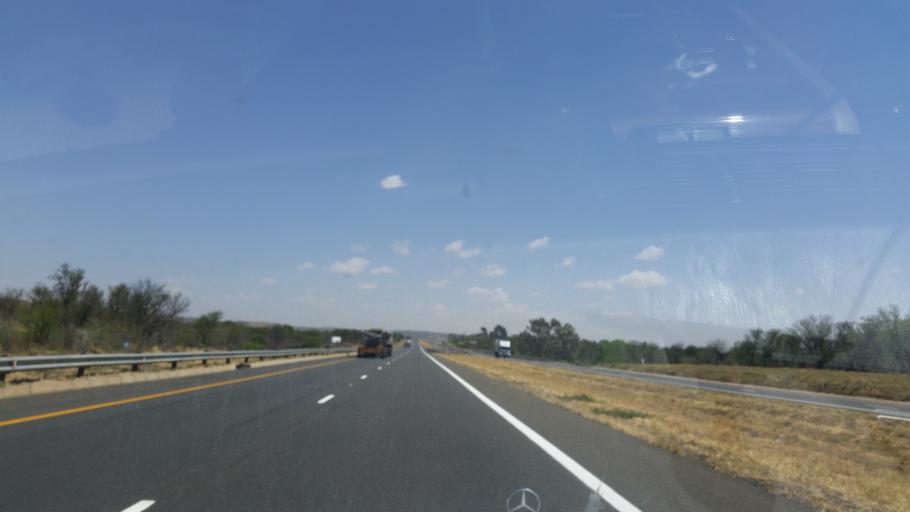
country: ZA
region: Orange Free State
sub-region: Mangaung Metropolitan Municipality
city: Bloemfontein
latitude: -28.9616
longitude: 26.3610
